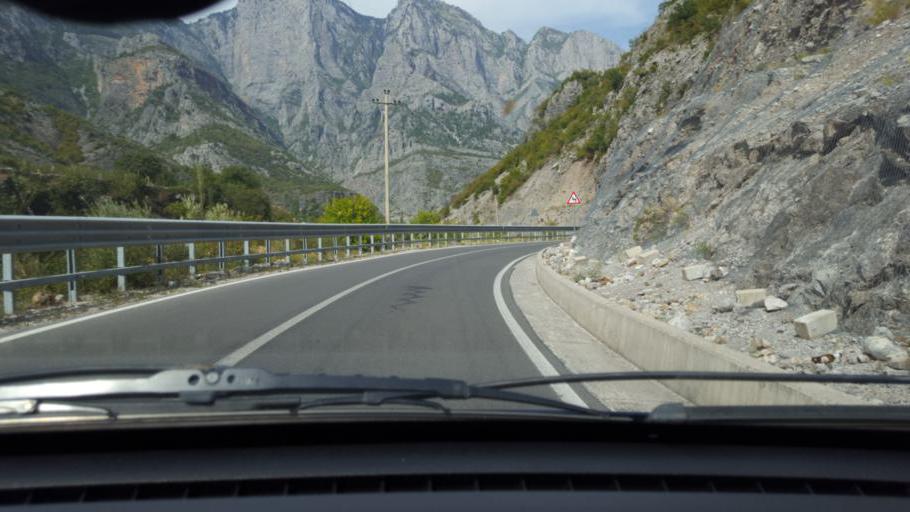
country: AL
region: Shkoder
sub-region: Rrethi i Malesia e Madhe
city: Kastrat
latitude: 42.4562
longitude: 19.5609
